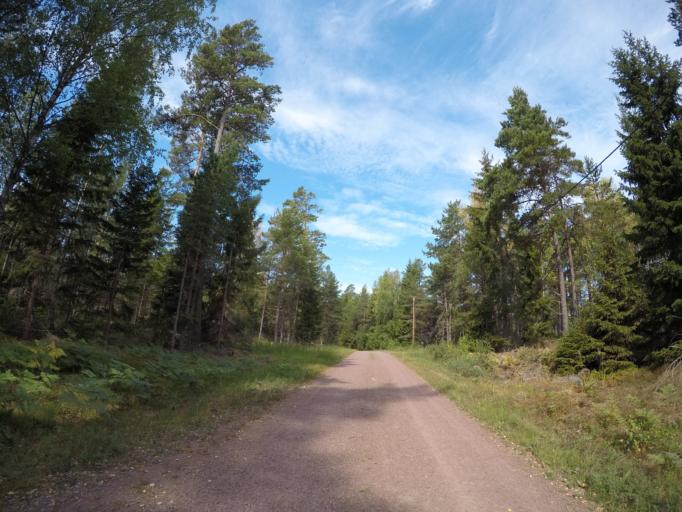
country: AX
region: Alands landsbygd
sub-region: Hammarland
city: Hammarland
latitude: 60.2257
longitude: 19.8427
